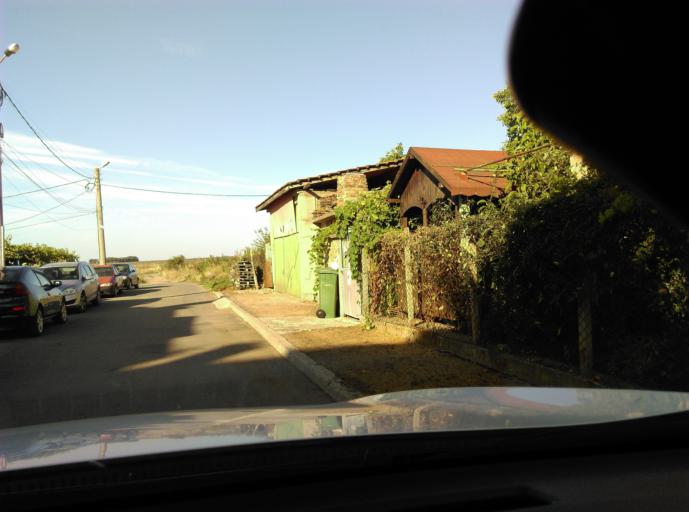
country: BG
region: Burgas
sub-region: Obshtina Kameno
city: Kameno
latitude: 42.5988
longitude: 27.3834
